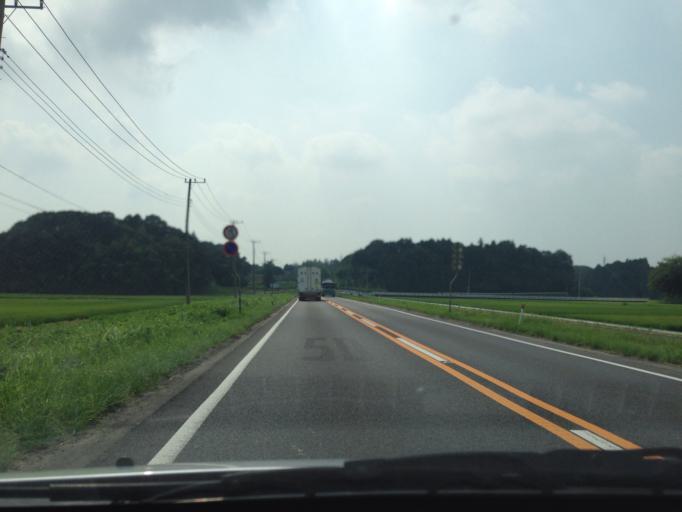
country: JP
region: Ibaraki
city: Inashiki
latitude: 36.0183
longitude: 140.2834
